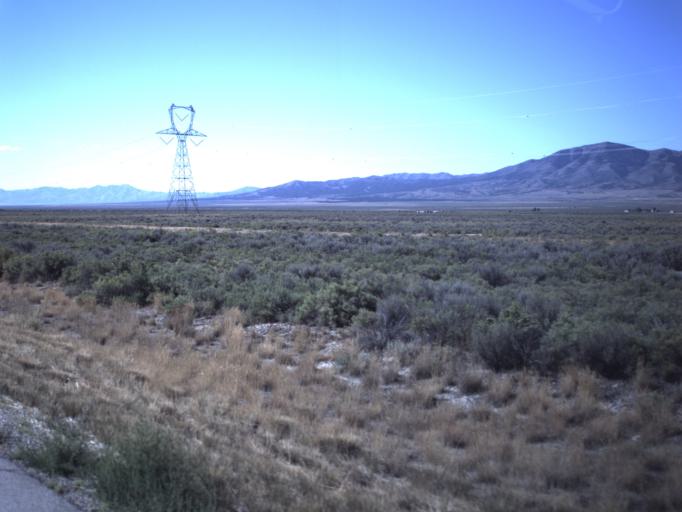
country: US
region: Utah
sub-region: Tooele County
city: Tooele
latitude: 40.3479
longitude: -112.4117
